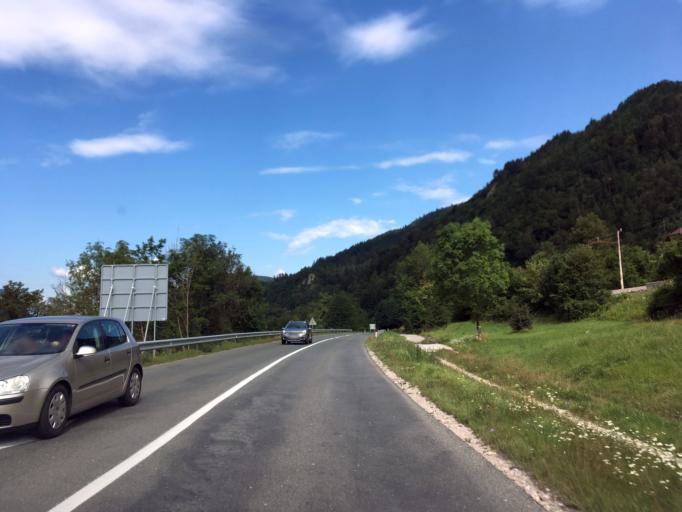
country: SI
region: Zirovnica
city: Zirovnica
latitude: 46.4116
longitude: 14.1286
